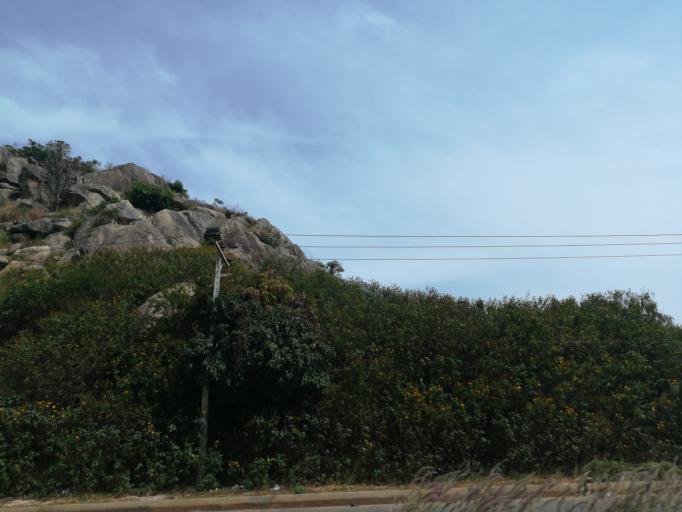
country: NG
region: Plateau
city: Bukuru
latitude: 9.8304
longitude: 8.8670
